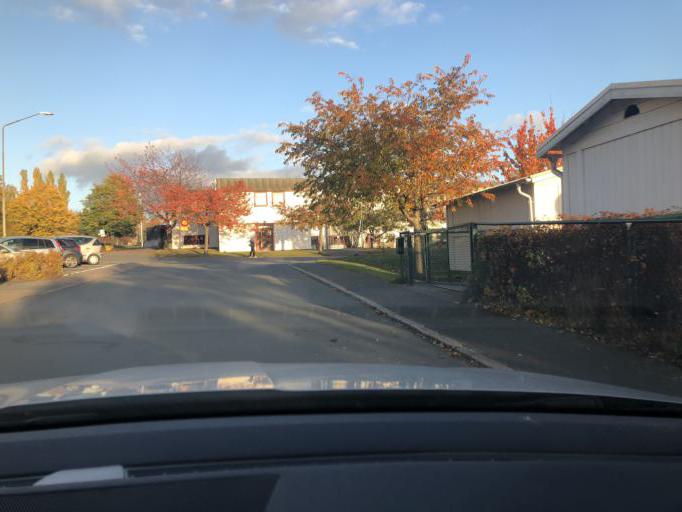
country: SE
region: Joenkoeping
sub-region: Jonkopings Kommun
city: Jonkoping
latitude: 57.7819
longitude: 14.2136
